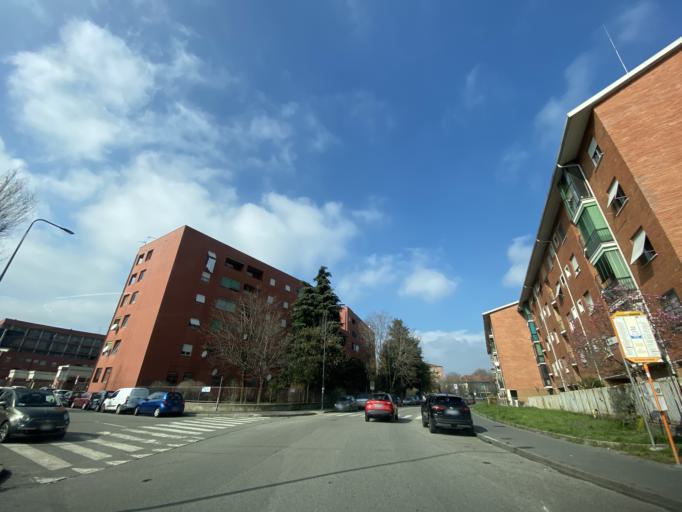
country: IT
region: Lombardy
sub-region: Citta metropolitana di Milano
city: Bresso
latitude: 45.5135
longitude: 9.1933
